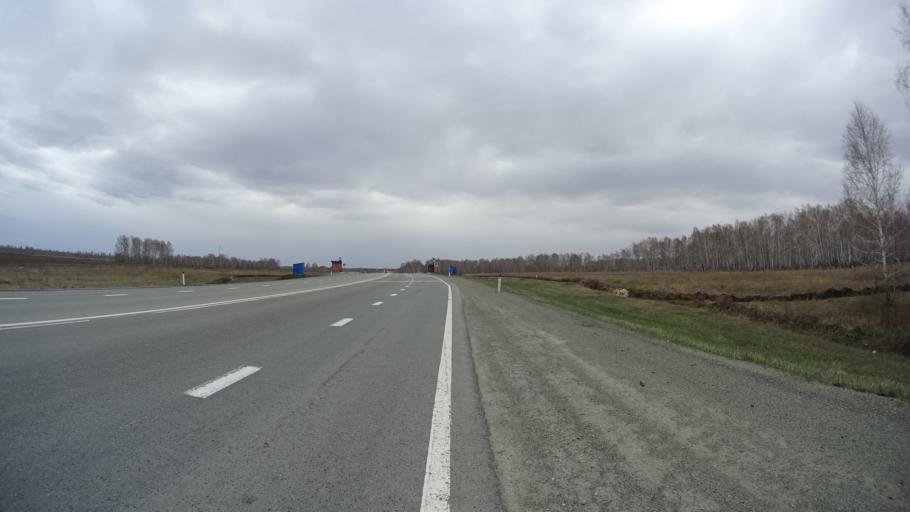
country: RU
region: Chelyabinsk
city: Yemanzhelinsk
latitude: 54.6973
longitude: 61.2502
